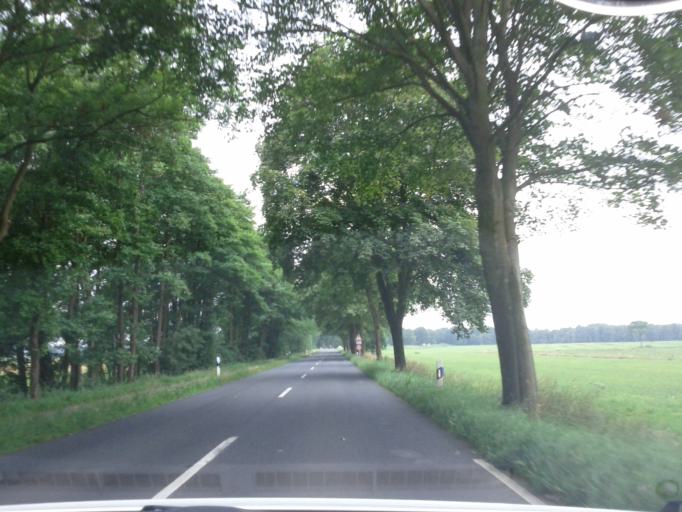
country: DE
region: Lower Saxony
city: Kranenburg
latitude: 53.6235
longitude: 9.1809
